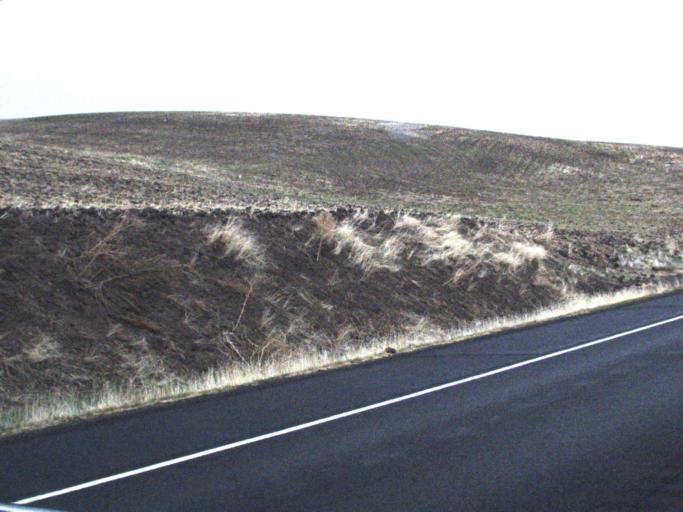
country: US
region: Washington
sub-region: Walla Walla County
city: Walla Walla East
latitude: 46.1250
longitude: -118.2007
